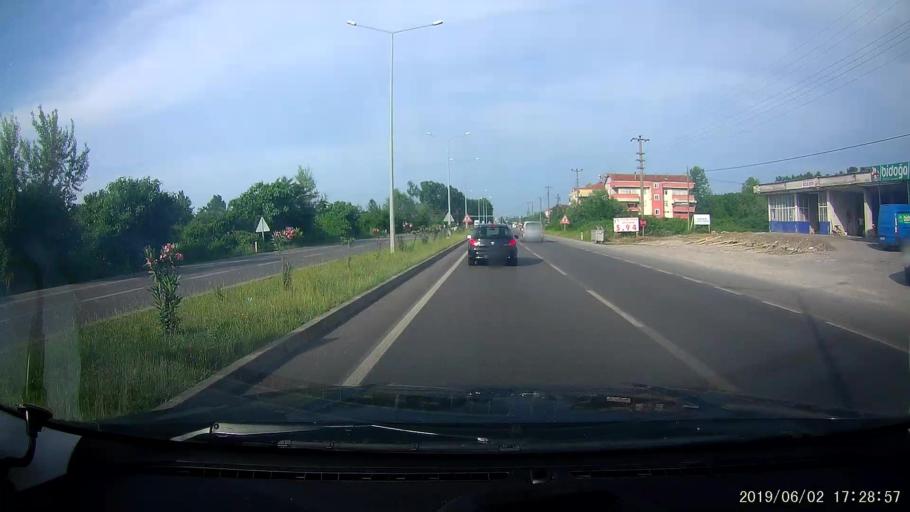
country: TR
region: Samsun
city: Carsamba
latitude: 41.2092
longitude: 36.7512
